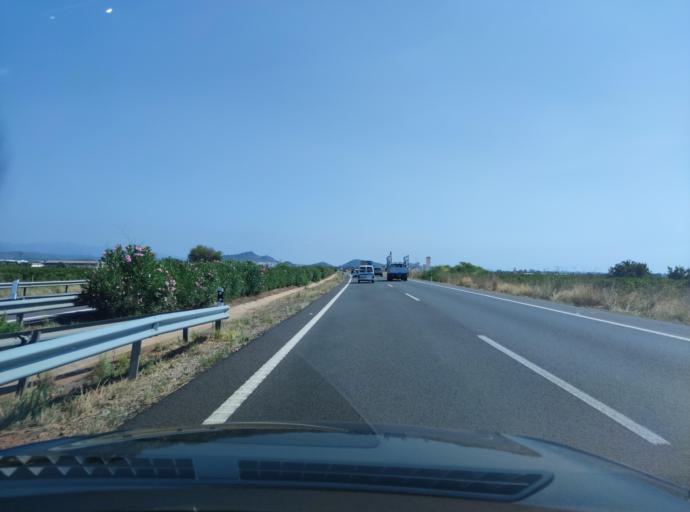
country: ES
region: Valencia
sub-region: Provincia de Valencia
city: Faura
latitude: 39.7107
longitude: -0.2399
